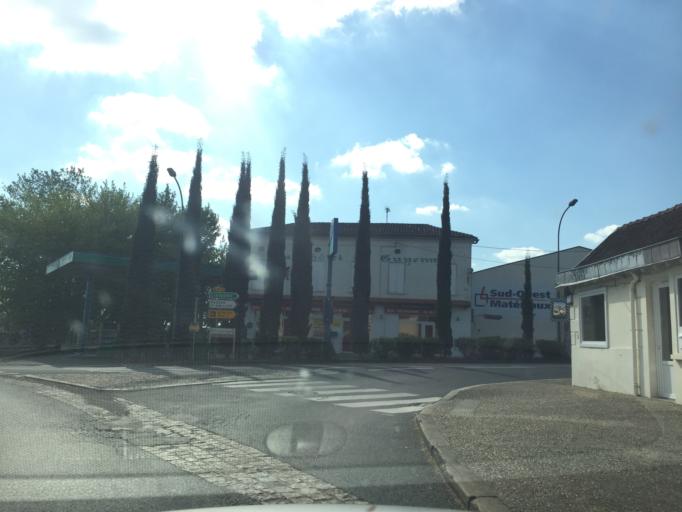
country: FR
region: Aquitaine
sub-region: Departement de la Gironde
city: Sauveterre-de-Guyenne
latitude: 44.6949
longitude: -0.0881
